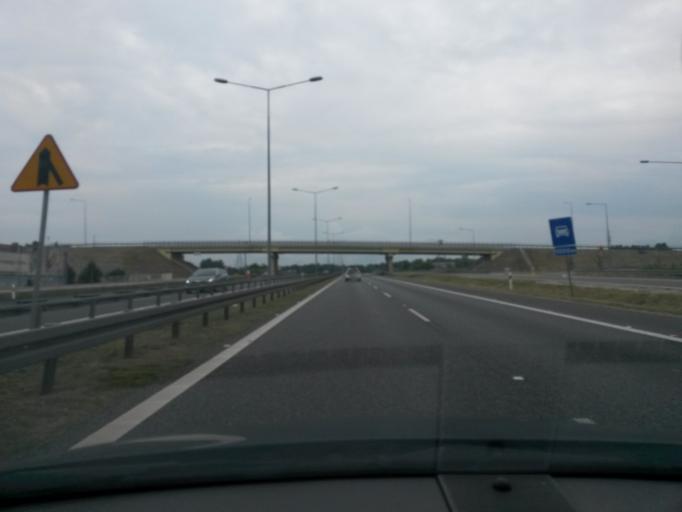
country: PL
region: Masovian Voivodeship
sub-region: Powiat zyrardowski
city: Mszczonow
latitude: 51.9389
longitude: 20.4794
